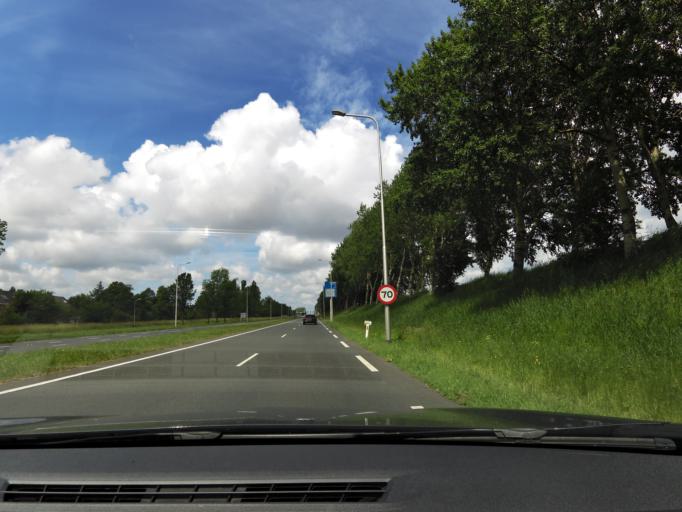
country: NL
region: Zeeland
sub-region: Gemeente Vlissingen
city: Vlissingen
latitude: 51.4591
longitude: 3.5903
